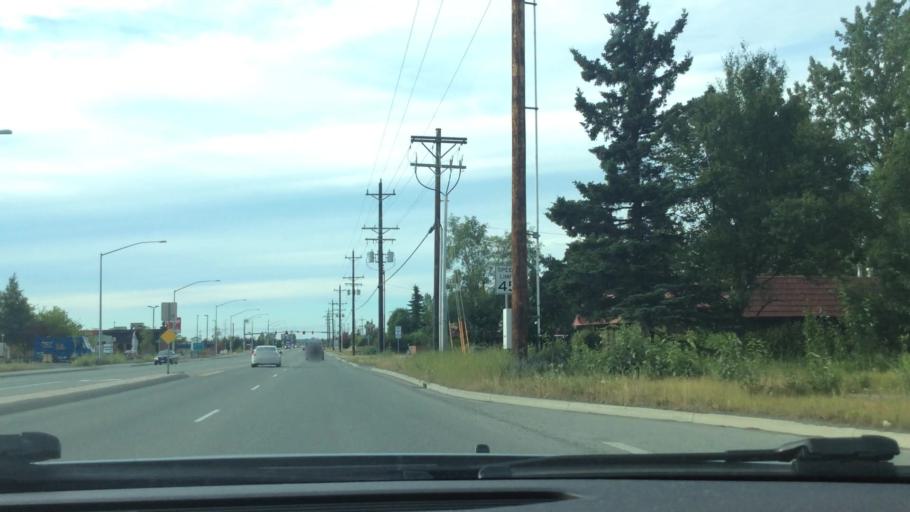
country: US
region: Alaska
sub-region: Anchorage Municipality
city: Anchorage
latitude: 61.1164
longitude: -149.8637
